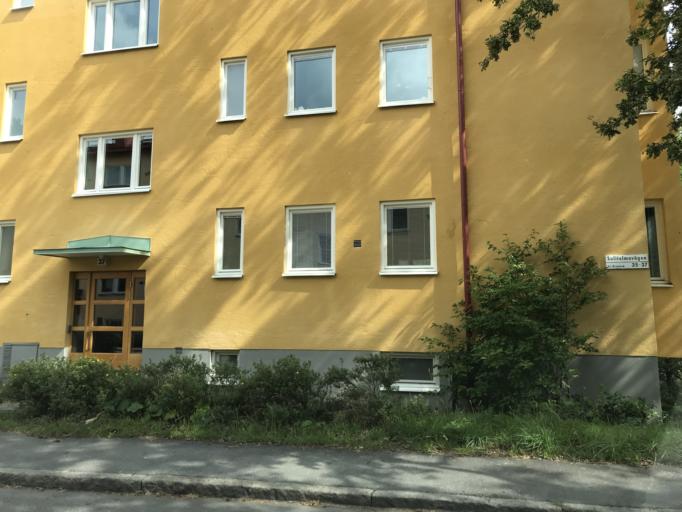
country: SE
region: Stockholm
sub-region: Sundbybergs Kommun
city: Sundbyberg
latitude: 59.3371
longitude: 17.9778
